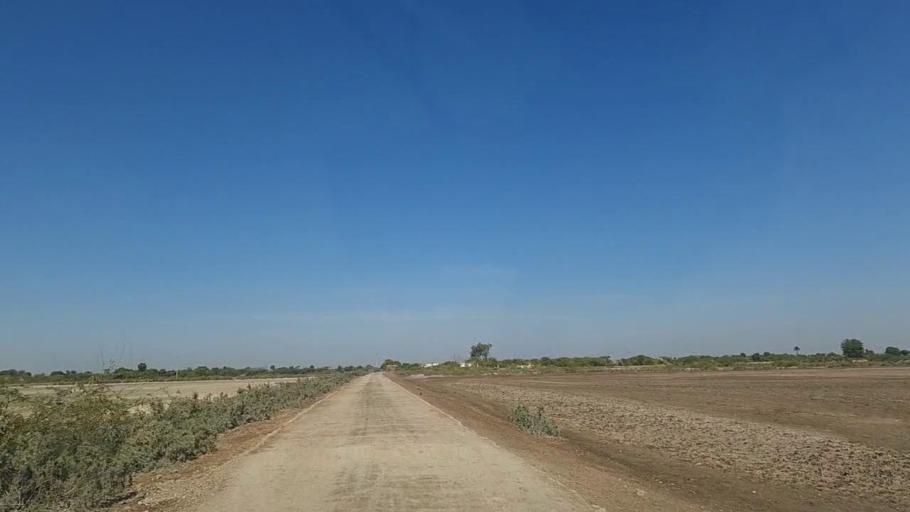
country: PK
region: Sindh
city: Samaro
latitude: 25.3058
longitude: 69.4858
